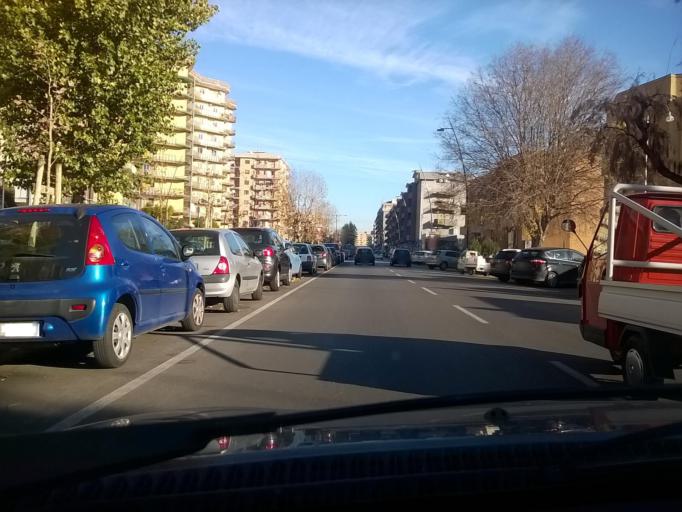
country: IT
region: Apulia
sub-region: Provincia di Taranto
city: Taranto
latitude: 40.4549
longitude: 17.2642
